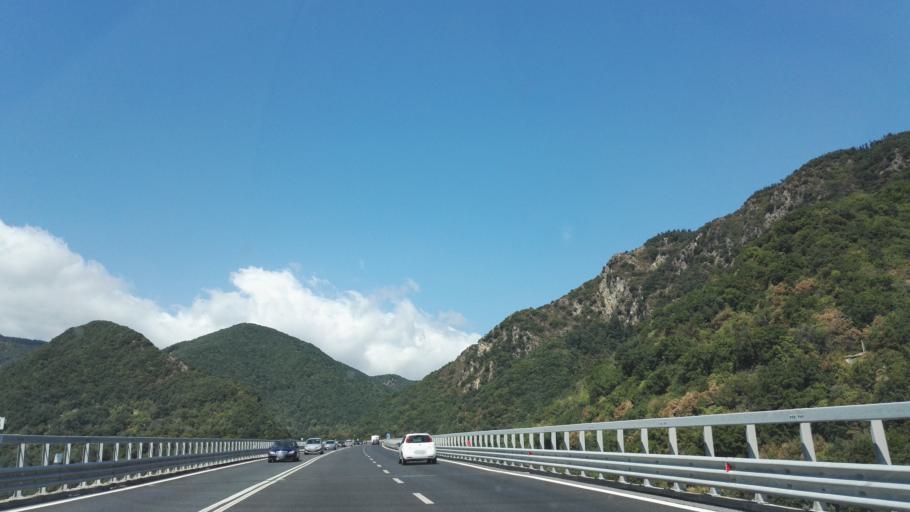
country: IT
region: Calabria
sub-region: Provincia di Reggio Calabria
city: Mammola
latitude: 38.3603
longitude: 16.2045
